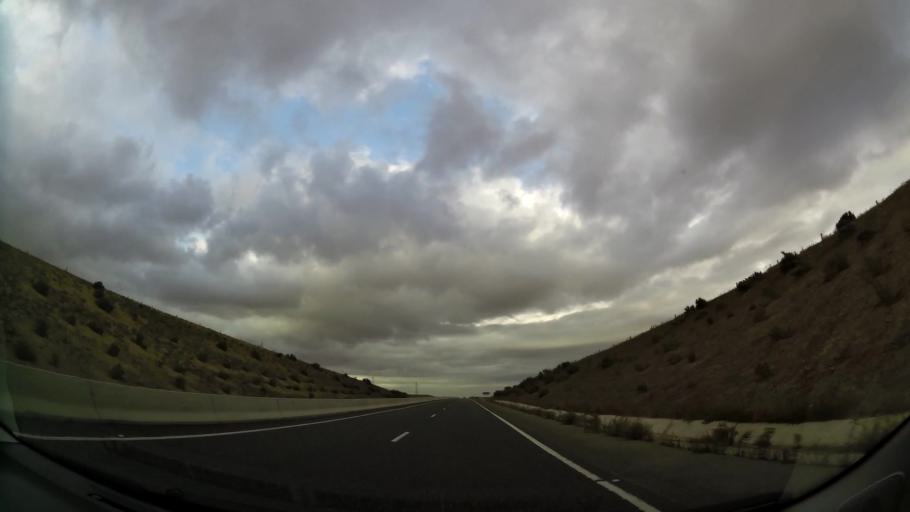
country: MA
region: Taza-Al Hoceima-Taounate
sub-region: Taza
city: Taza
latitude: 34.2689
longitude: -3.8211
